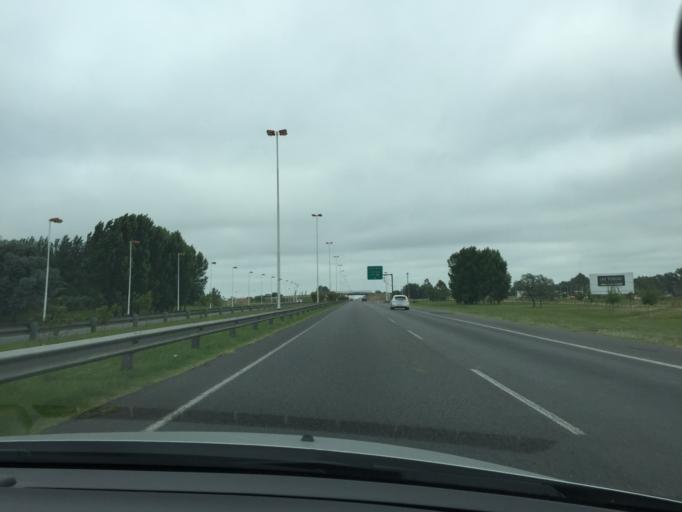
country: AR
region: Buenos Aires
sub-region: Partido de Ezeiza
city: Ezeiza
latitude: -34.8725
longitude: -58.5824
